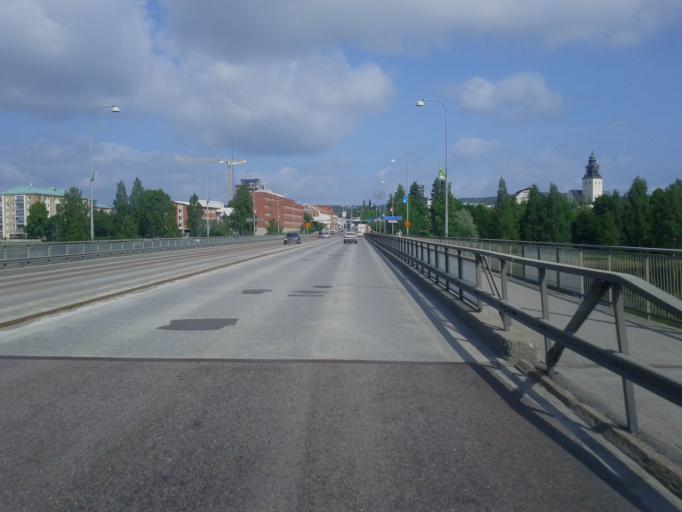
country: SE
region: Vaesterbotten
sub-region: Skelleftea Kommun
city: Skelleftea
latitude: 64.7462
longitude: 20.9598
